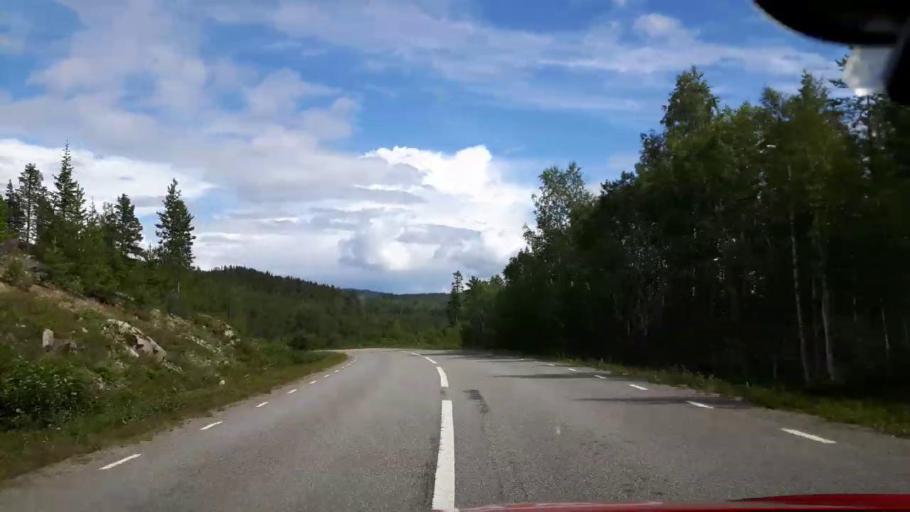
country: SE
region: Jaemtland
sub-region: Stroemsunds Kommun
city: Stroemsund
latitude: 64.3419
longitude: 15.1150
